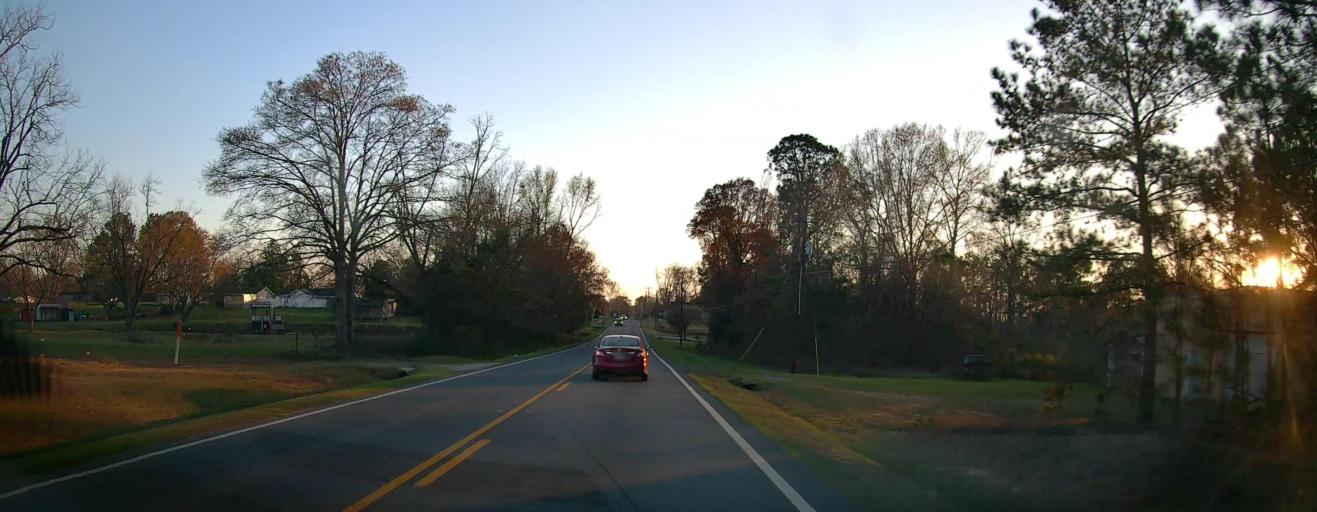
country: US
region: Georgia
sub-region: Dodge County
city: Chester
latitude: 32.3434
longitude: -83.0395
